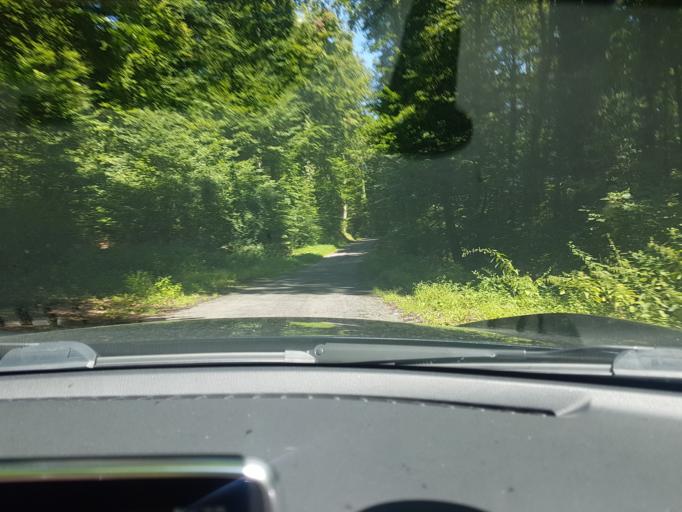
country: DE
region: Baden-Wuerttemberg
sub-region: Karlsruhe Region
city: Neckarzimmern
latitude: 49.3200
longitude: 9.1481
